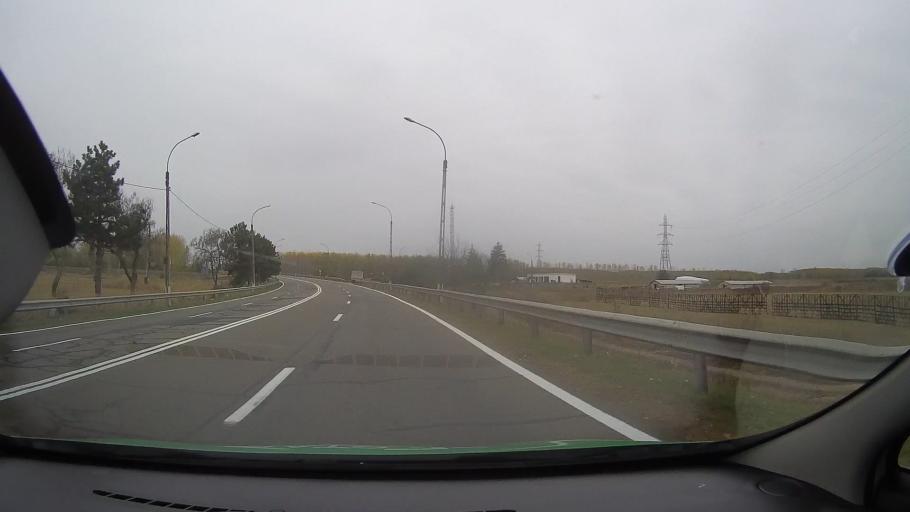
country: RO
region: Ialomita
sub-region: Comuna Giurgeni
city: Giurgeni
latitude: 44.7509
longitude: 27.8917
